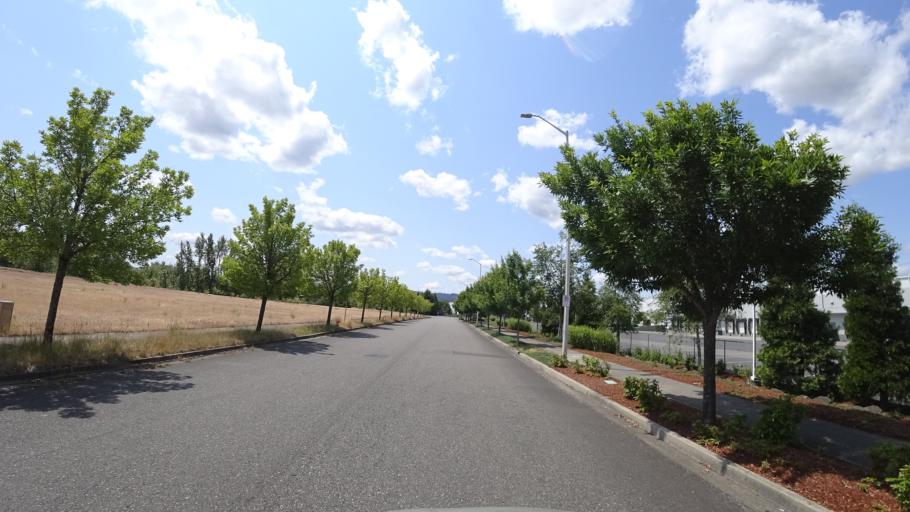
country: US
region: Washington
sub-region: Clark County
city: Lake Shore
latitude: 45.6302
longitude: -122.7550
